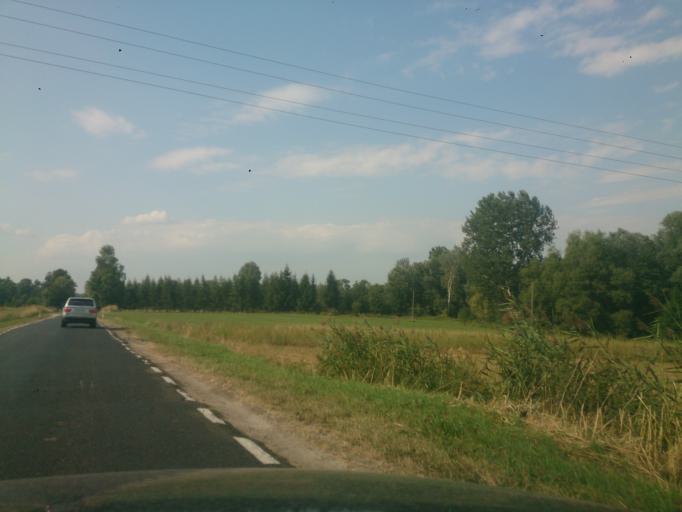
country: PL
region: Swietokrzyskie
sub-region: Powiat sandomierski
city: Klimontow
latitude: 50.6842
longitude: 21.3861
